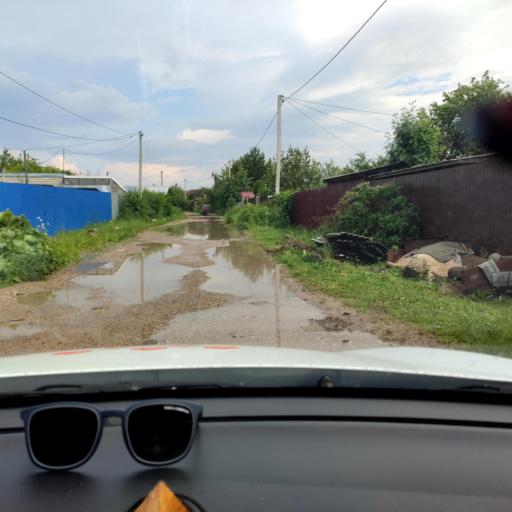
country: RU
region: Tatarstan
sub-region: Zelenodol'skiy Rayon
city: Vasil'yevo
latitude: 55.8229
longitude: 48.7259
